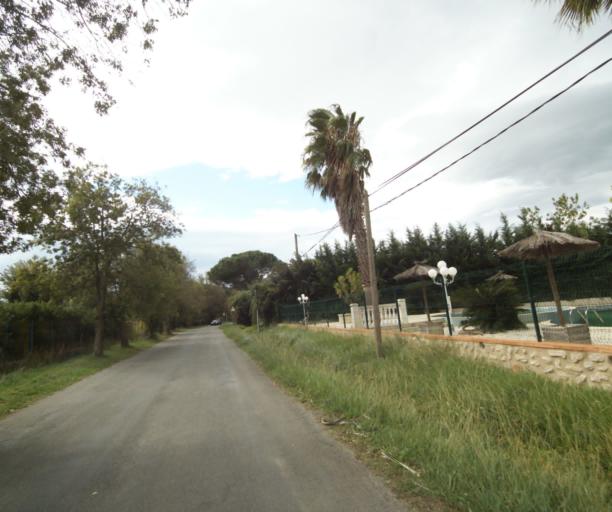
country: FR
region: Languedoc-Roussillon
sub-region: Departement des Pyrenees-Orientales
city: Argelers
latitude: 42.5691
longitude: 3.0341
